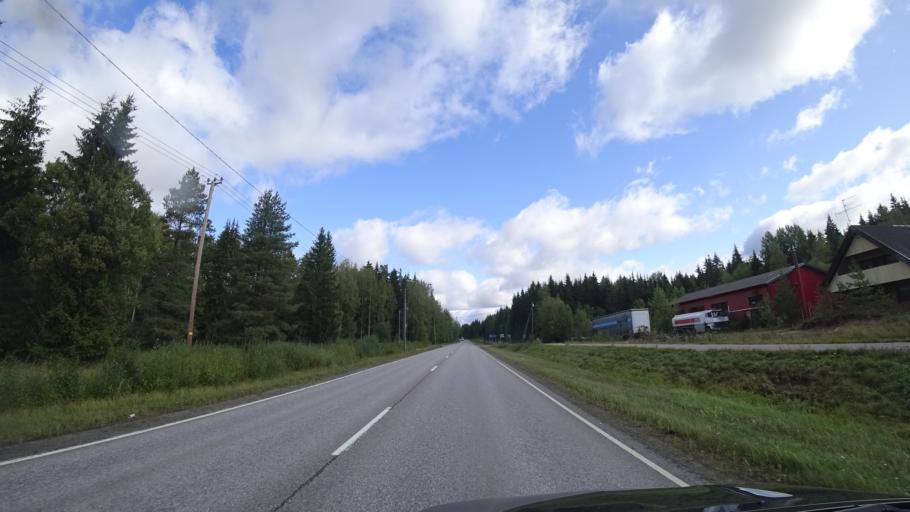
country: FI
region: Uusimaa
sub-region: Helsinki
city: Hyvinge
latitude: 60.5673
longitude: 24.9756
